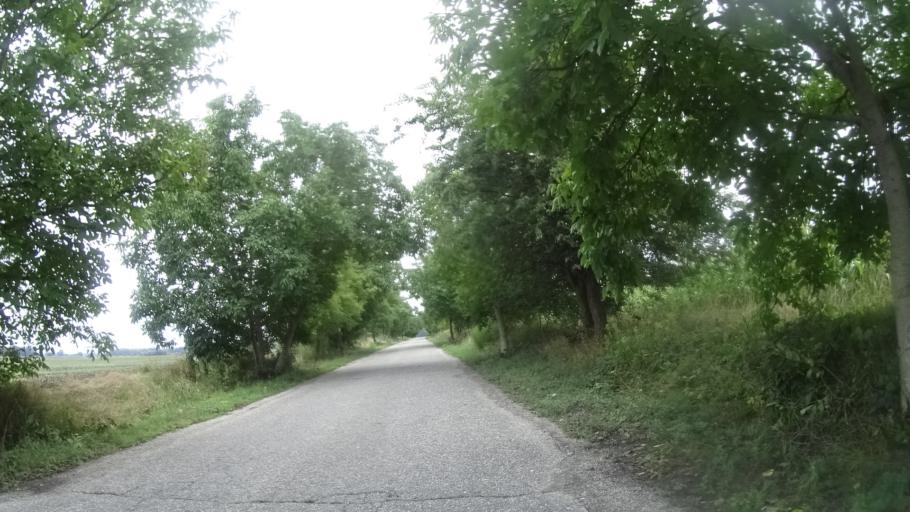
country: HU
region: Komarom-Esztergom
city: Acs
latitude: 47.7662
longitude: 17.9541
